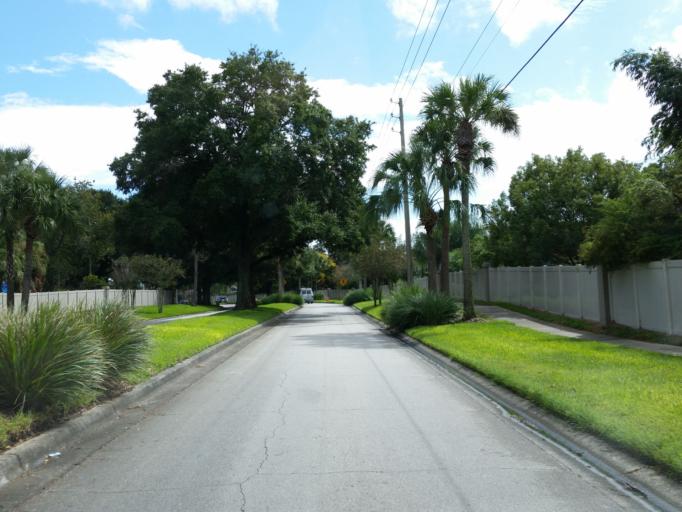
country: US
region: Florida
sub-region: Hillsborough County
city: Brandon
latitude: 27.9291
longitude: -82.2628
